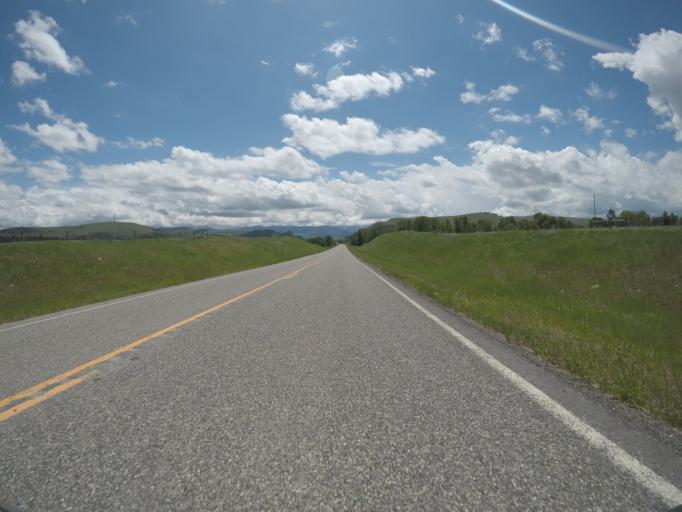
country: US
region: Montana
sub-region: Sweet Grass County
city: Big Timber
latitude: 45.6640
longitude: -110.1129
